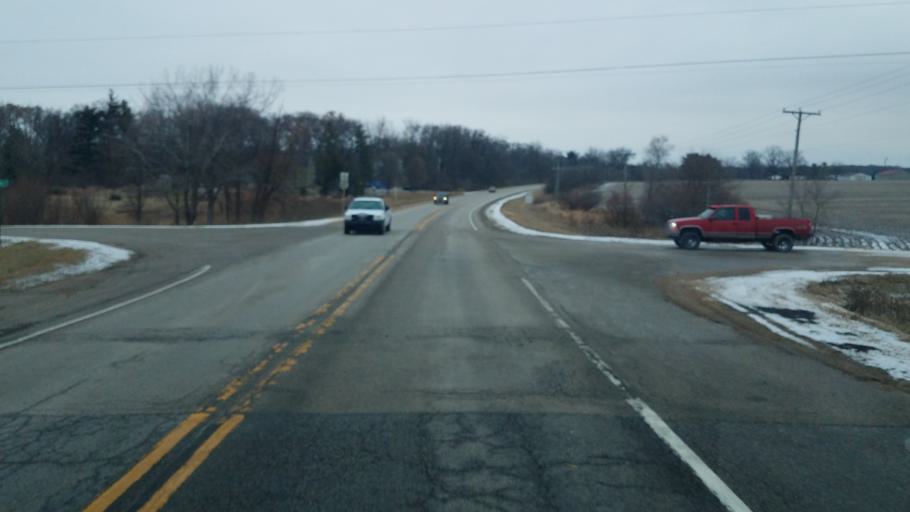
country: US
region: Illinois
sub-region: Kane County
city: Sugar Grove
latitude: 41.8228
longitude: -88.4676
